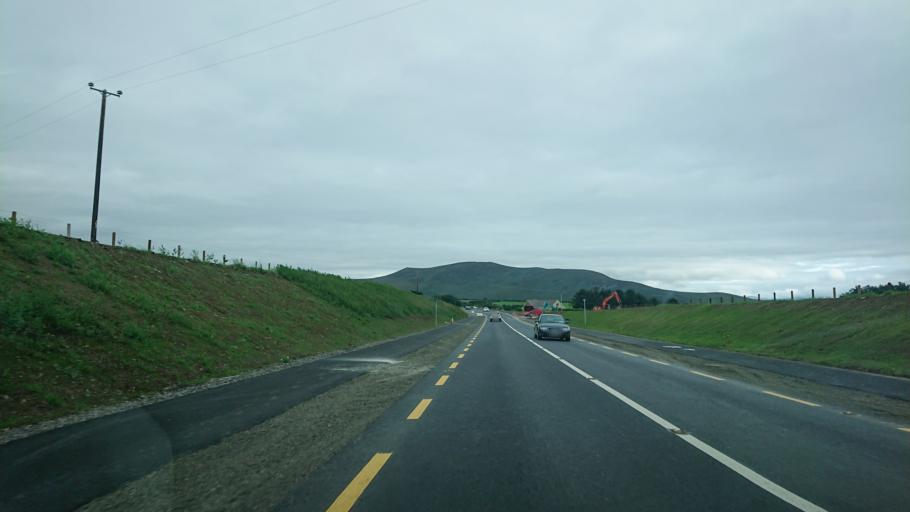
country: IE
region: Munster
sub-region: Ciarrai
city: Dingle
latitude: 52.1444
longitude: -10.1212
